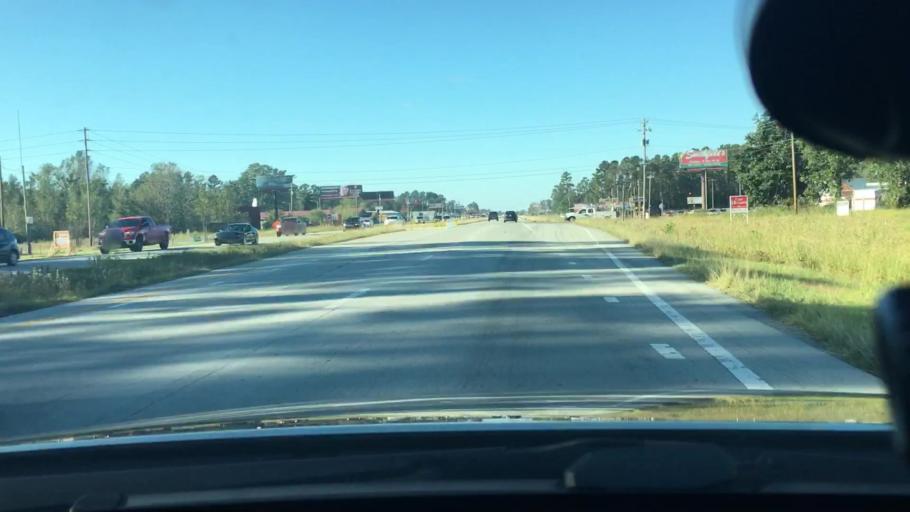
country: US
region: North Carolina
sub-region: Craven County
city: James City
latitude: 35.0555
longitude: -77.0171
